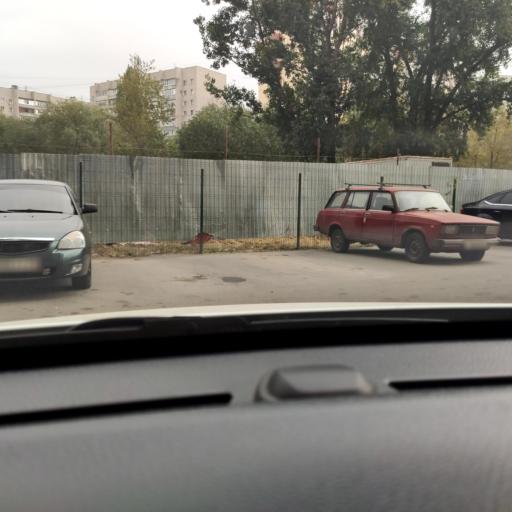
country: RU
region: Voronezj
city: Voronezh
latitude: 51.7064
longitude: 39.2718
